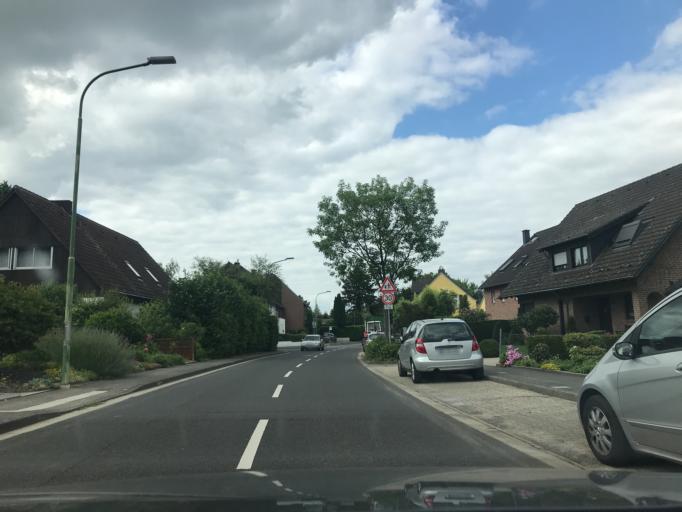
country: DE
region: North Rhine-Westphalia
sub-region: Regierungsbezirk Dusseldorf
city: Neuss
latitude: 51.1410
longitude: 6.7216
